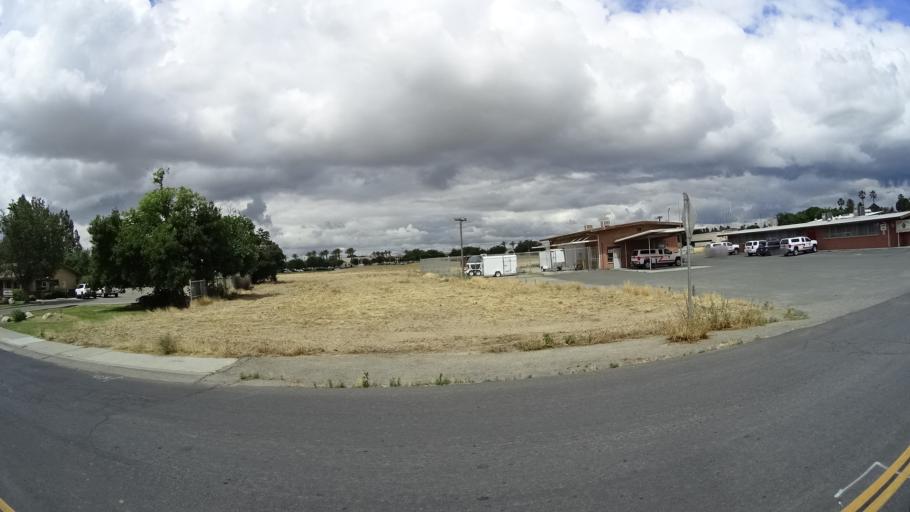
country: US
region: California
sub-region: Kings County
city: Hanford
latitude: 36.3259
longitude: -119.6641
